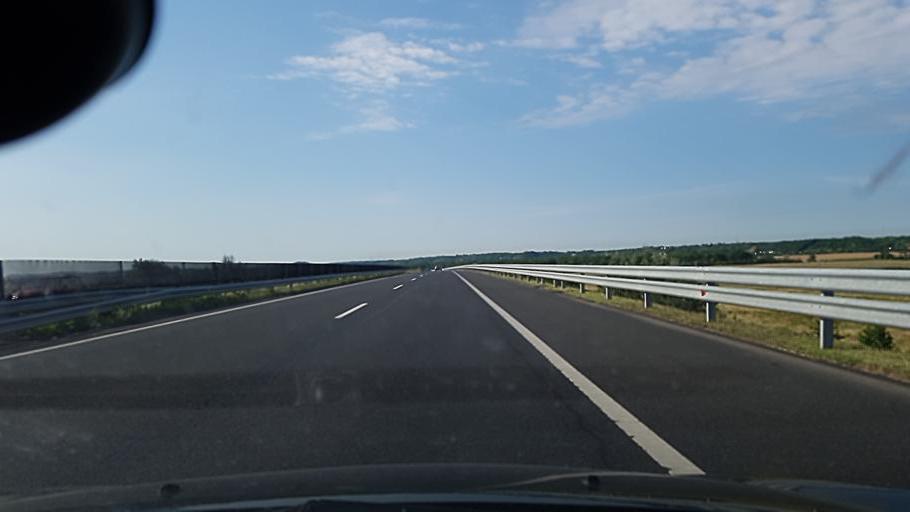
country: HU
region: Fejer
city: Adony
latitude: 47.1084
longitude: 18.8418
